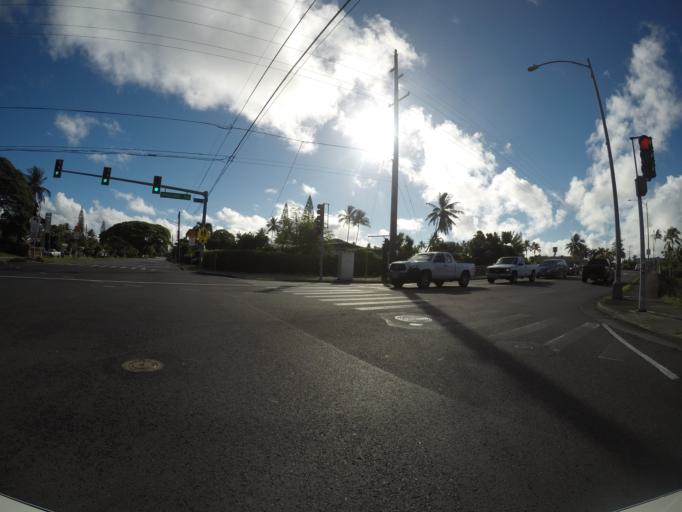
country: US
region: Hawaii
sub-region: Honolulu County
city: Kailua
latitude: 21.4095
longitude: -157.7550
